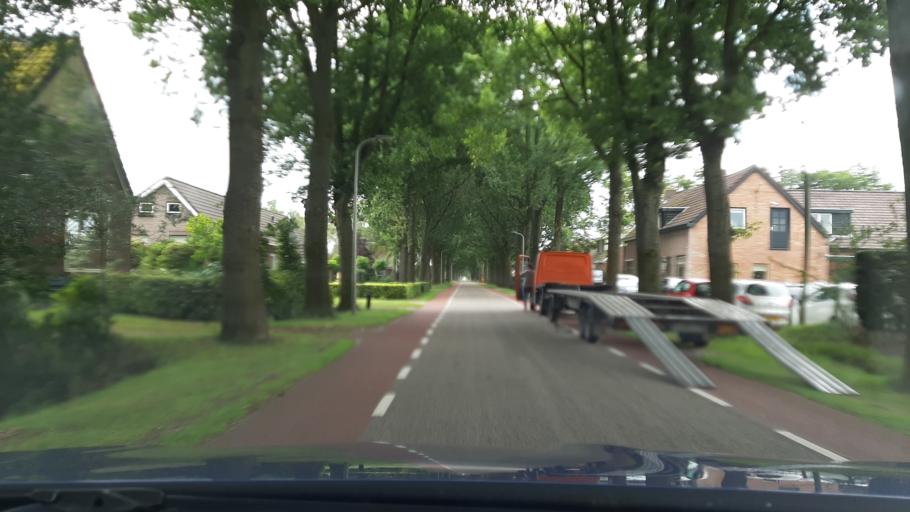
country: NL
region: Drenthe
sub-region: Gemeente Hoogeveen
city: Hoogeveen
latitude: 52.6892
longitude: 6.5384
